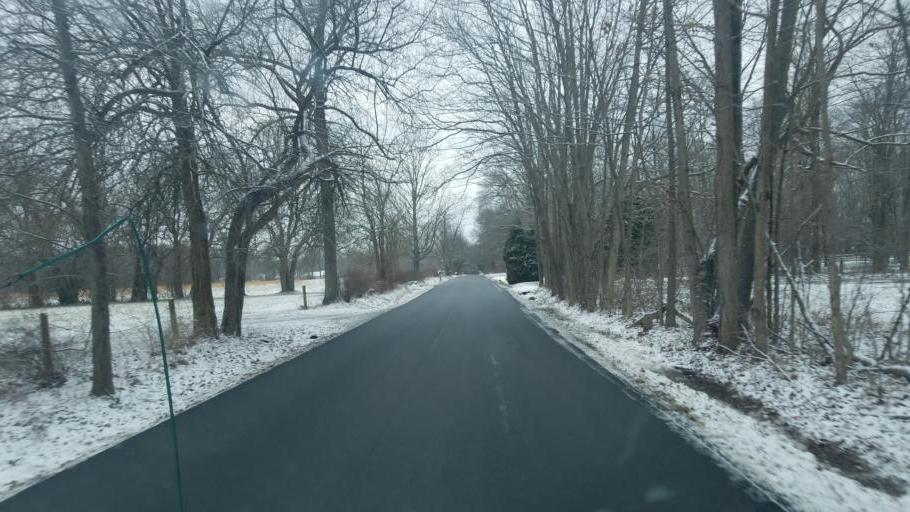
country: US
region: Ohio
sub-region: Franklin County
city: Gahanna
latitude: 40.0316
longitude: -82.8316
